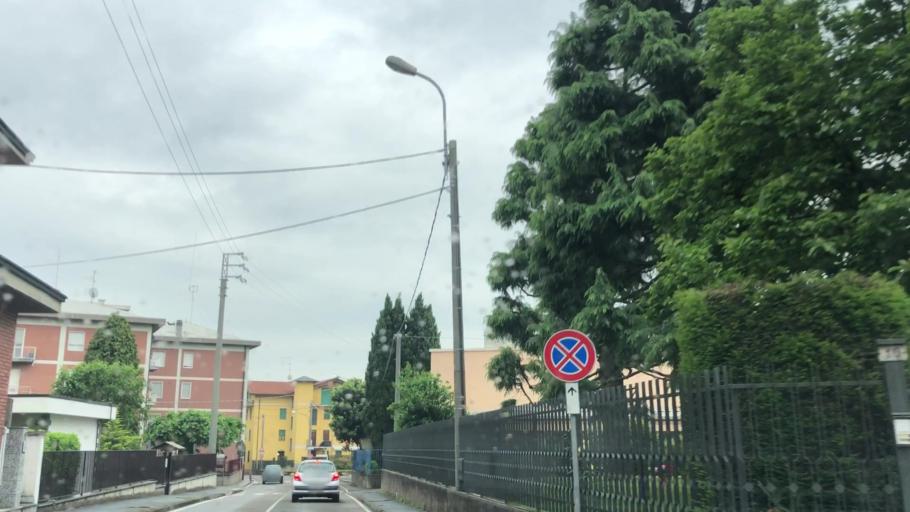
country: IT
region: Lombardy
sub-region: Provincia di Como
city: Limido Comasco
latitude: 45.6904
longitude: 8.9822
